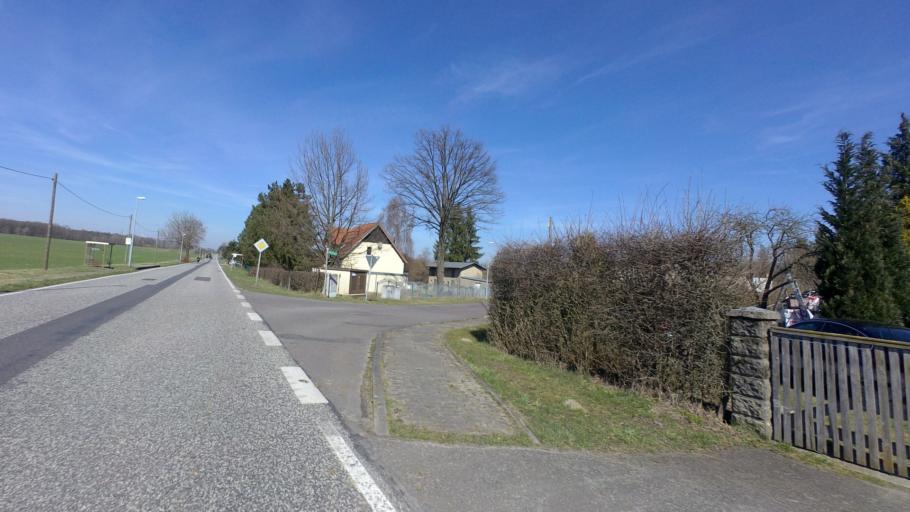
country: DE
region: Brandenburg
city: Furstenwalde
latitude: 52.4084
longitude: 14.0451
